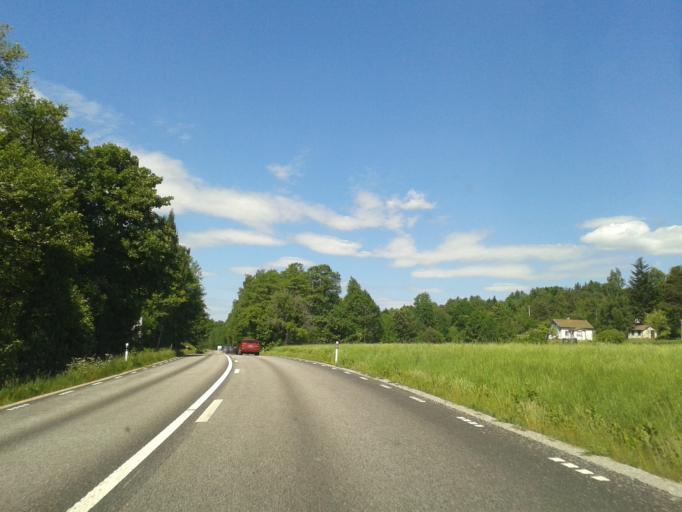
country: SE
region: Vaestra Goetaland
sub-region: Orust
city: Henan
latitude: 58.3163
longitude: 11.6858
